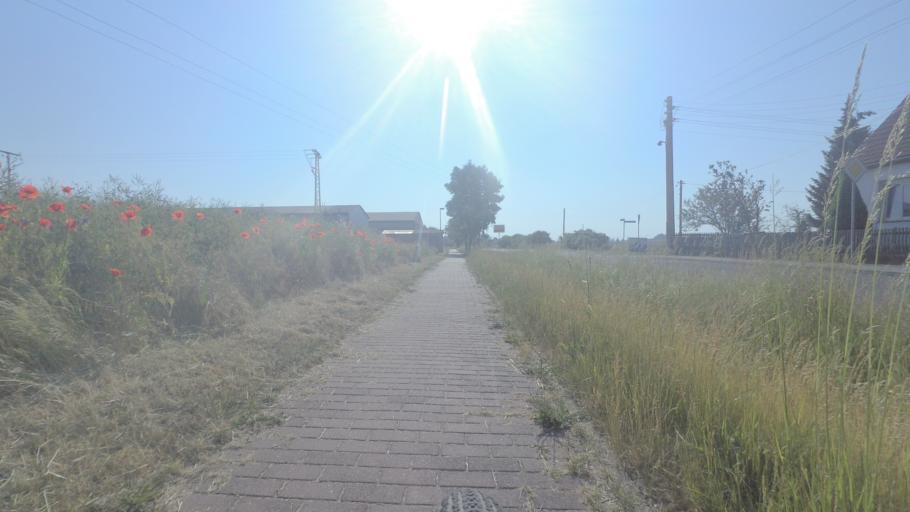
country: DE
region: Saxony-Anhalt
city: Osternienburg
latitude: 51.7922
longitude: 12.0369
